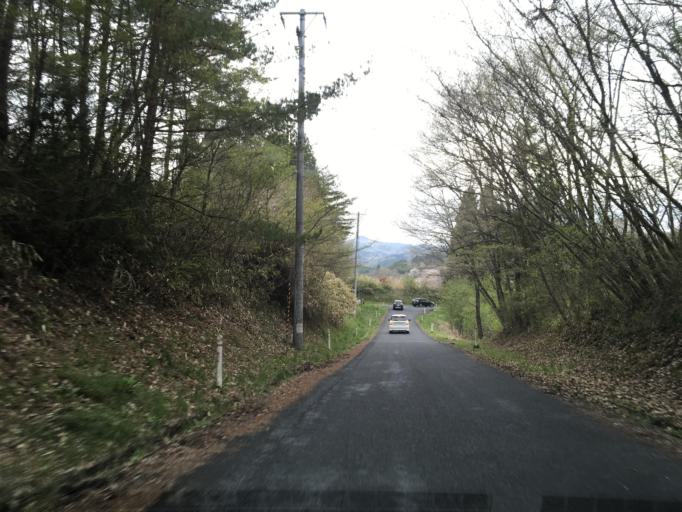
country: JP
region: Iwate
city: Ichinoseki
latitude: 38.8477
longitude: 141.3301
